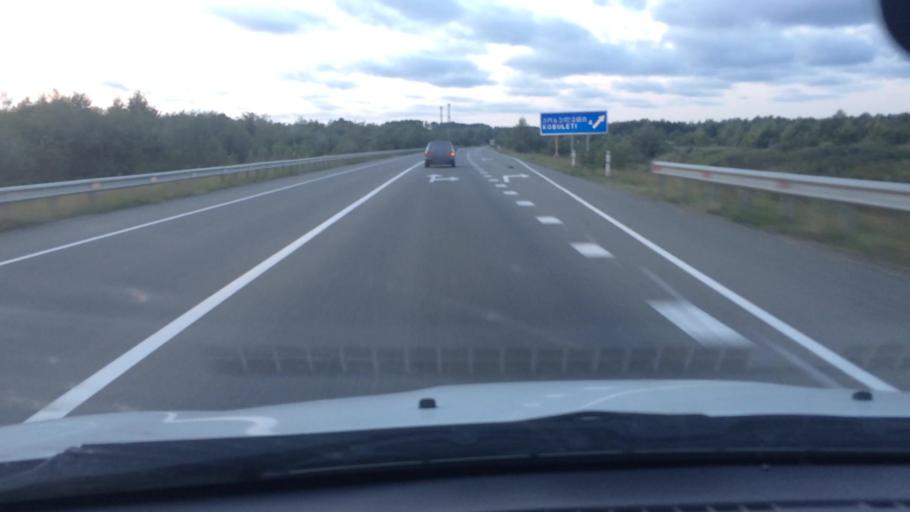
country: GE
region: Guria
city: Urek'i
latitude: 41.9189
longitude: 41.7755
